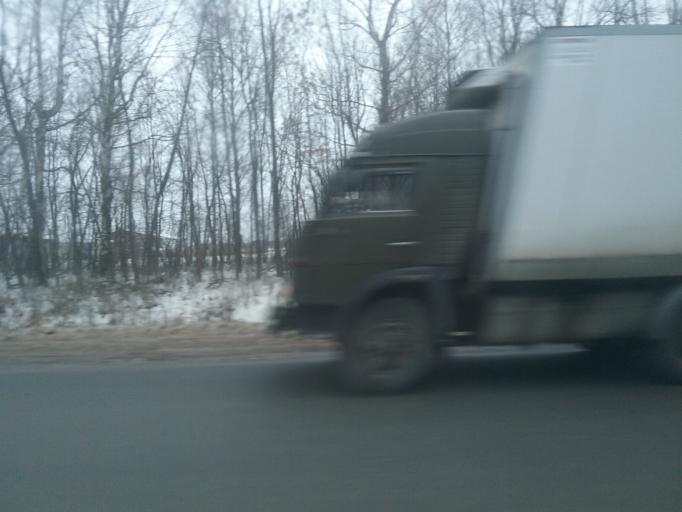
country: RU
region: Tula
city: Bolokhovo
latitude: 54.0407
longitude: 37.8672
